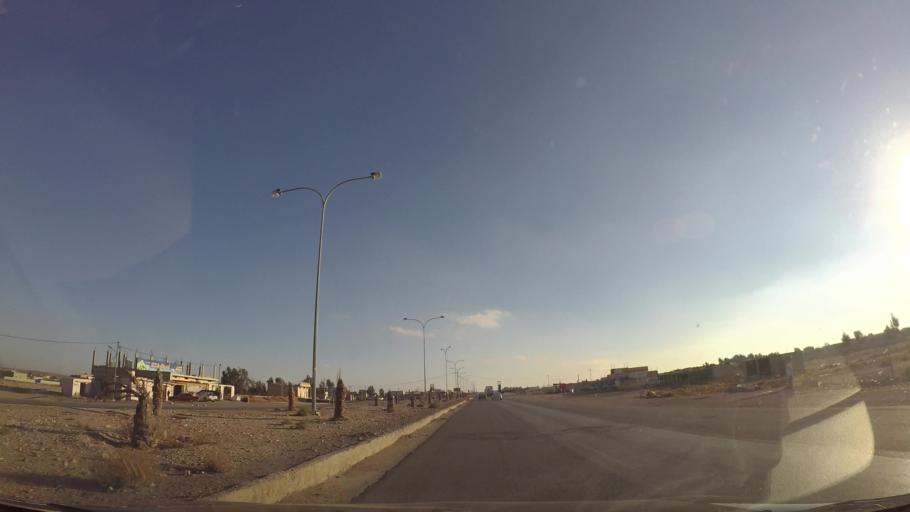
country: JO
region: Tafielah
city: Busayra
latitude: 30.5940
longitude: 35.8034
